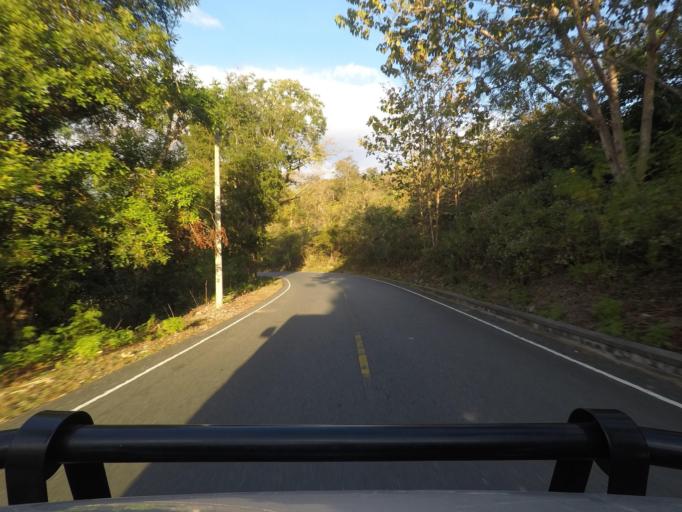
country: TL
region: Bobonaro
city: Maliana
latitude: -8.9485
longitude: 125.0943
